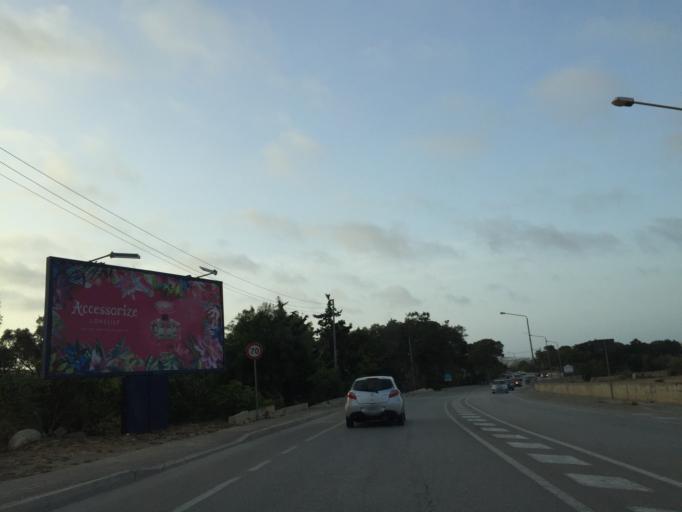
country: MT
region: Il-Mosta
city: Mosta
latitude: 35.9227
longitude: 14.4154
